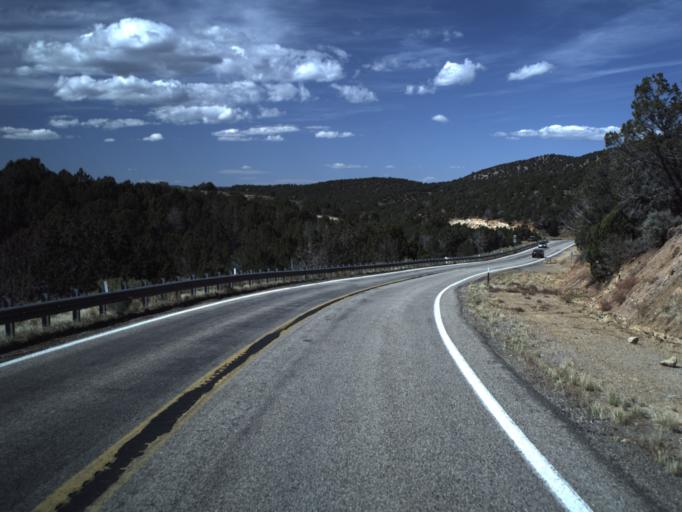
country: US
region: Utah
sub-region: Washington County
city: Enterprise
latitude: 37.5355
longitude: -113.6532
